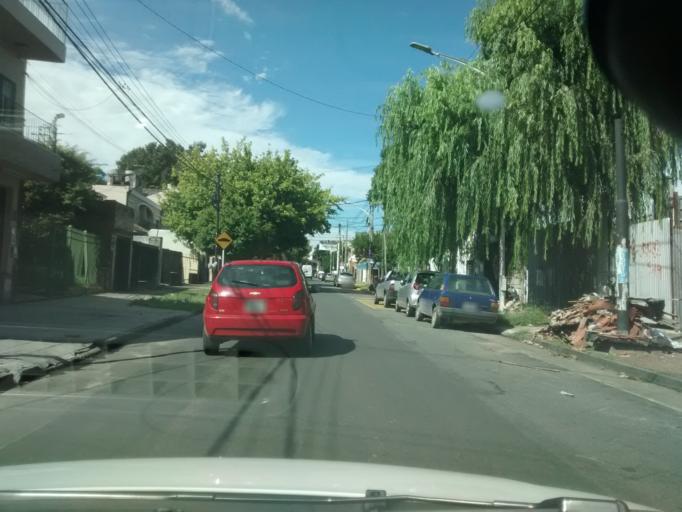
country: AR
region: Buenos Aires
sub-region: Partido de Moron
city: Moron
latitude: -34.6587
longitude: -58.6228
